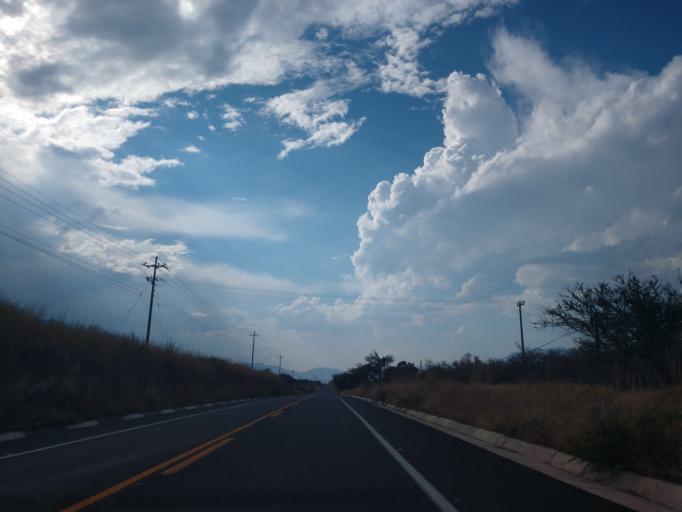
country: MX
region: Jalisco
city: Ajijic
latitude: 20.1905
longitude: -103.2577
